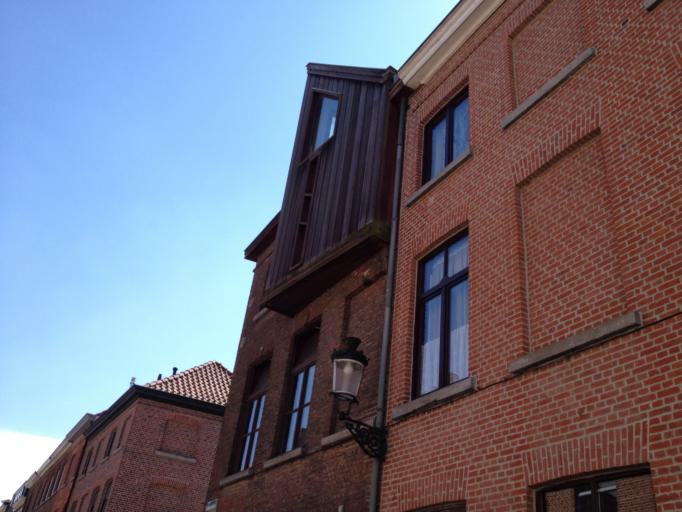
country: BE
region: Flanders
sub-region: Provincie West-Vlaanderen
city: Brugge
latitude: 51.2028
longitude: 3.2151
